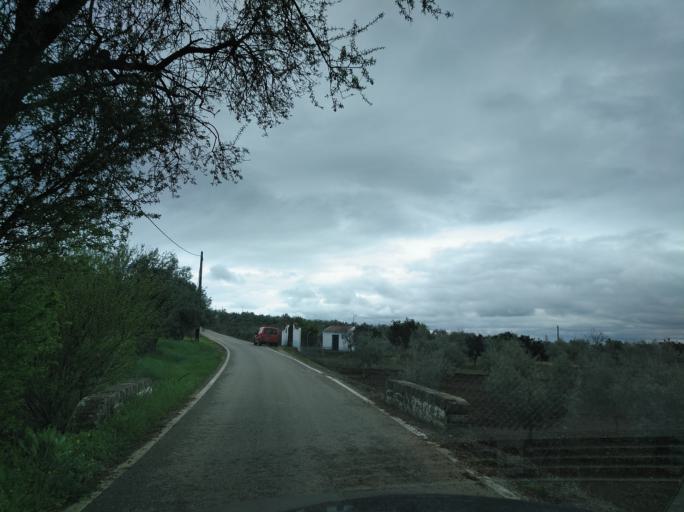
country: PT
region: Portalegre
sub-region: Campo Maior
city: Campo Maior
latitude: 38.9945
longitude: -7.0499
